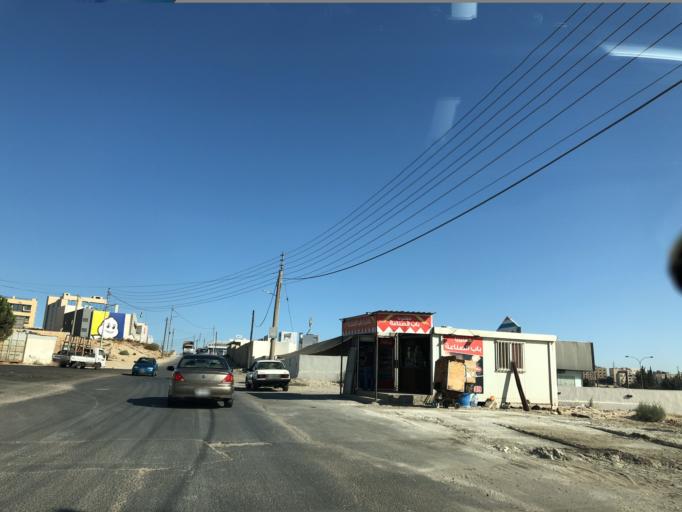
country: JO
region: Amman
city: Wadi as Sir
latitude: 31.9392
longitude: 35.8485
